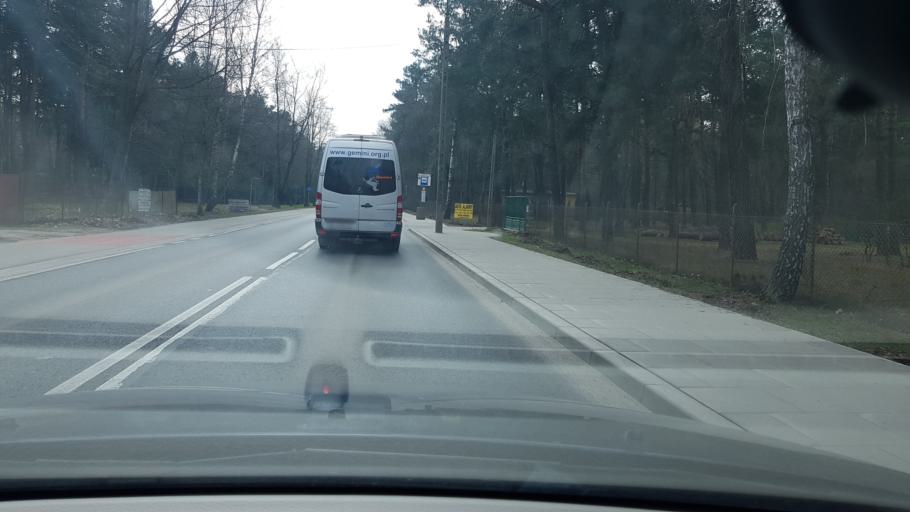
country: PL
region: Masovian Voivodeship
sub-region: Warszawa
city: Wesola
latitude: 52.2394
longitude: 21.2223
